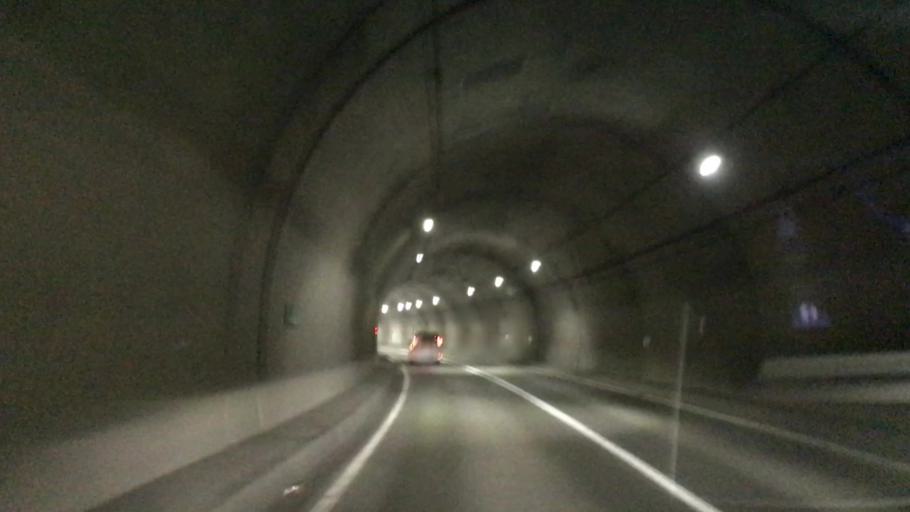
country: JP
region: Hokkaido
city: Shimo-furano
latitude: 42.9541
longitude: 142.6056
